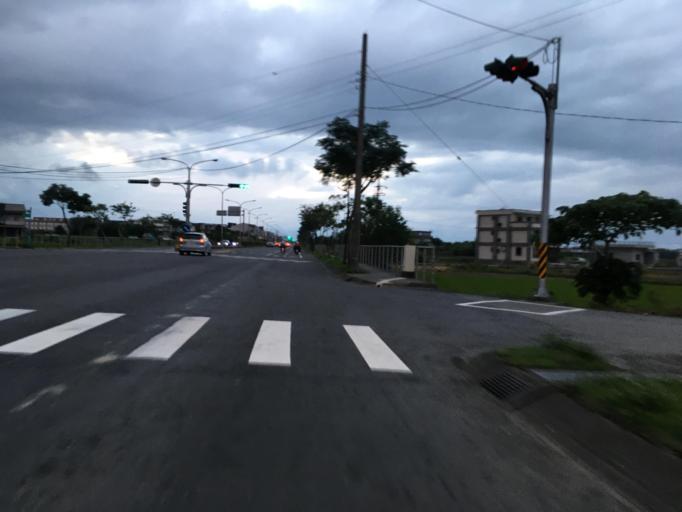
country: TW
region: Taiwan
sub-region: Yilan
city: Yilan
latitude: 24.6190
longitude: 121.8440
